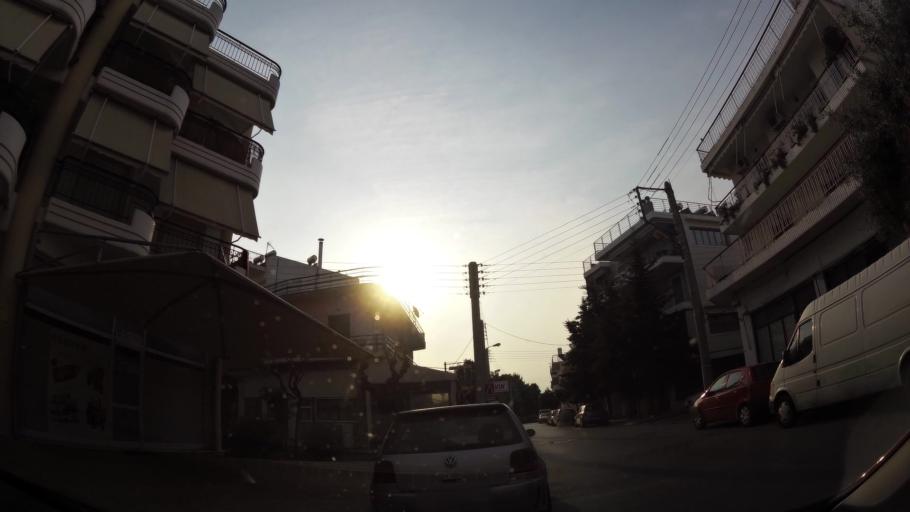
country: GR
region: Attica
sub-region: Nomarchia Athinas
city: Ilion
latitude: 38.0245
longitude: 23.7012
